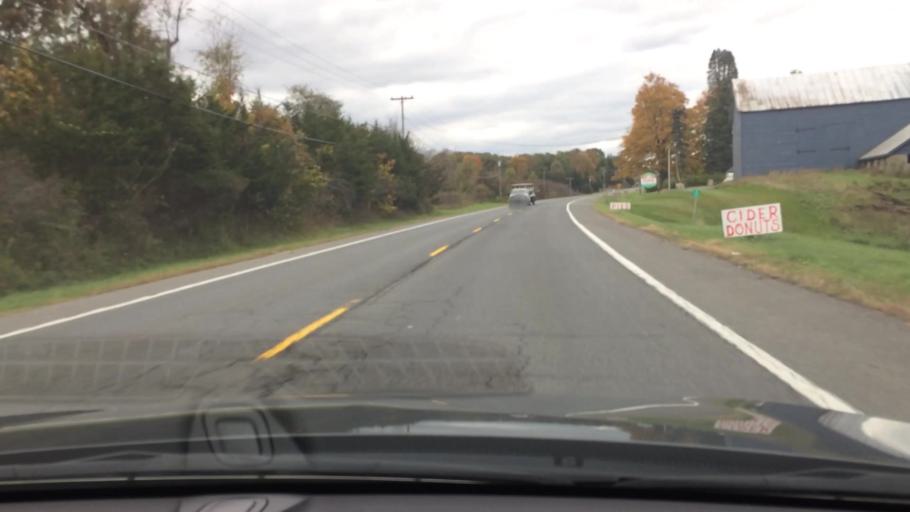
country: US
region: New York
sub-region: Columbia County
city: Oakdale
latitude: 42.1648
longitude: -73.7502
